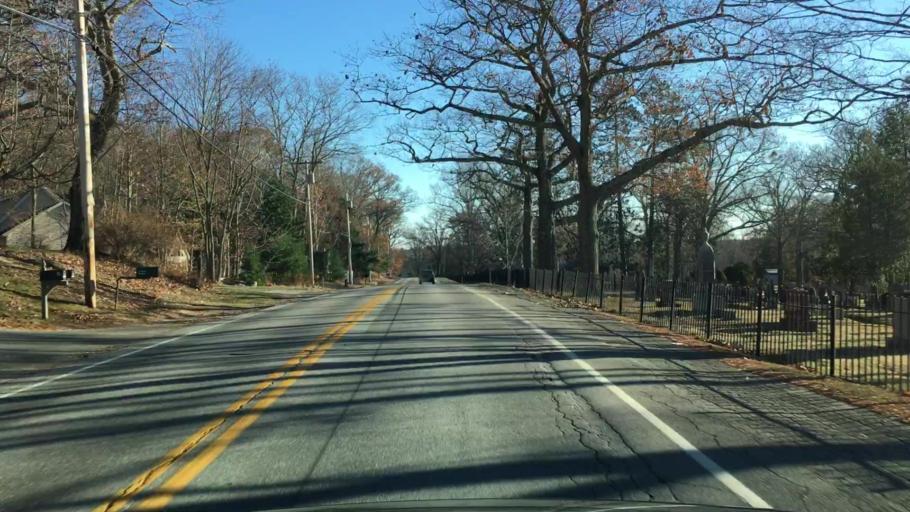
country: US
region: Maine
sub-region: Knox County
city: Camden
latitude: 44.2190
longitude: -69.0737
